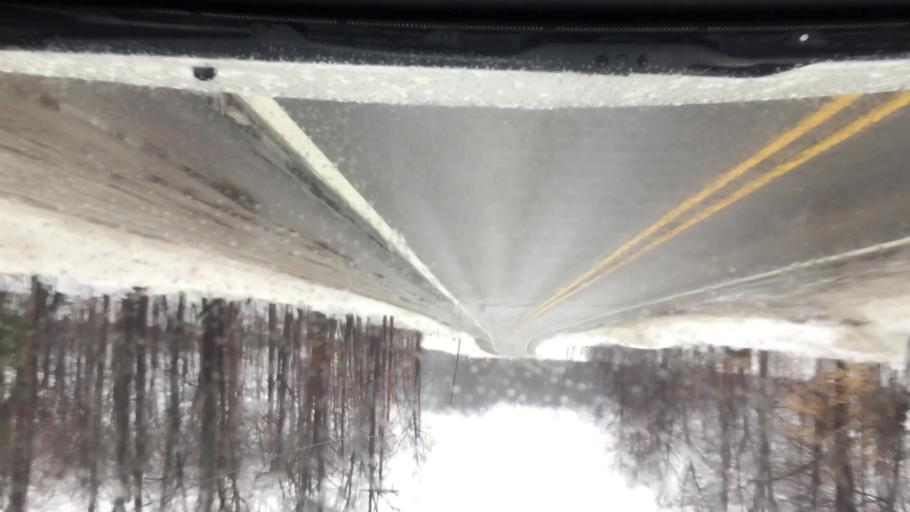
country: US
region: Michigan
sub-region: Charlevoix County
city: East Jordan
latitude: 45.2057
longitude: -85.1654
